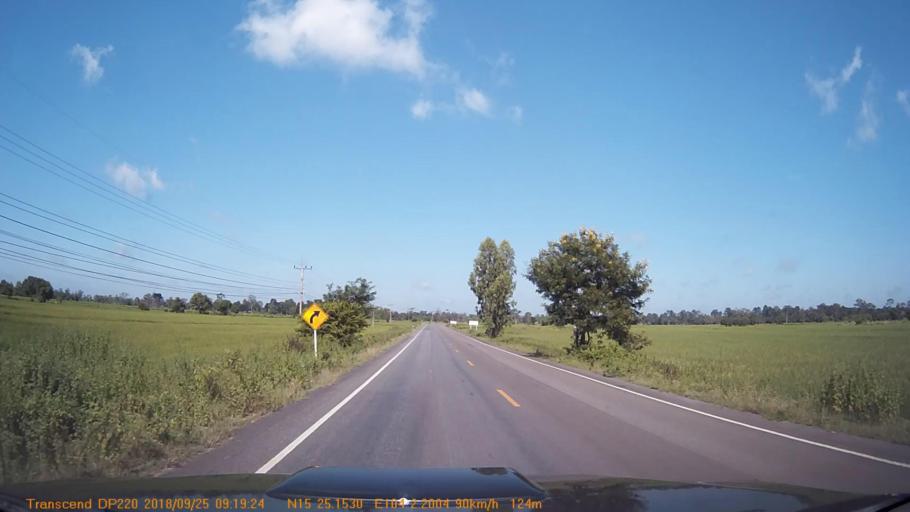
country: TH
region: Sisaket
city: Sila Lat
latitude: 15.4192
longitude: 104.0368
